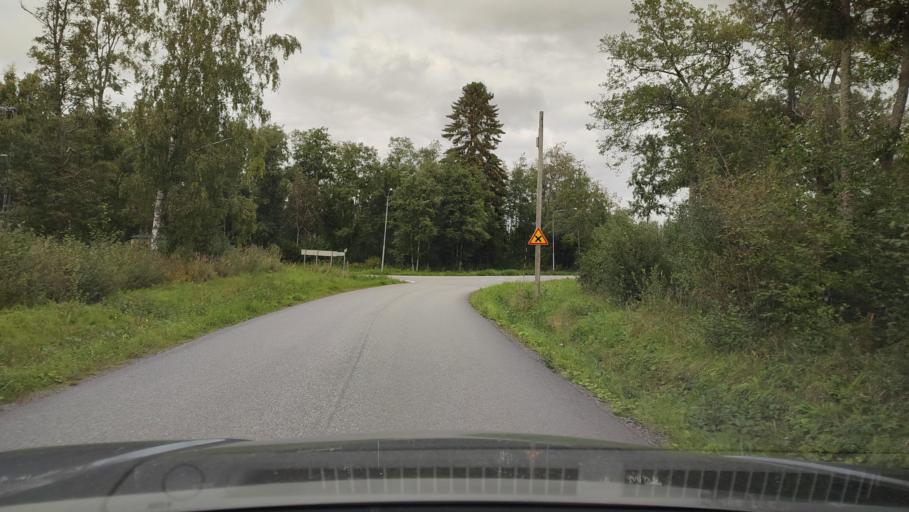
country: FI
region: Ostrobothnia
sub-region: Sydosterbotten
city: Kristinestad
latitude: 62.2635
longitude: 21.3609
